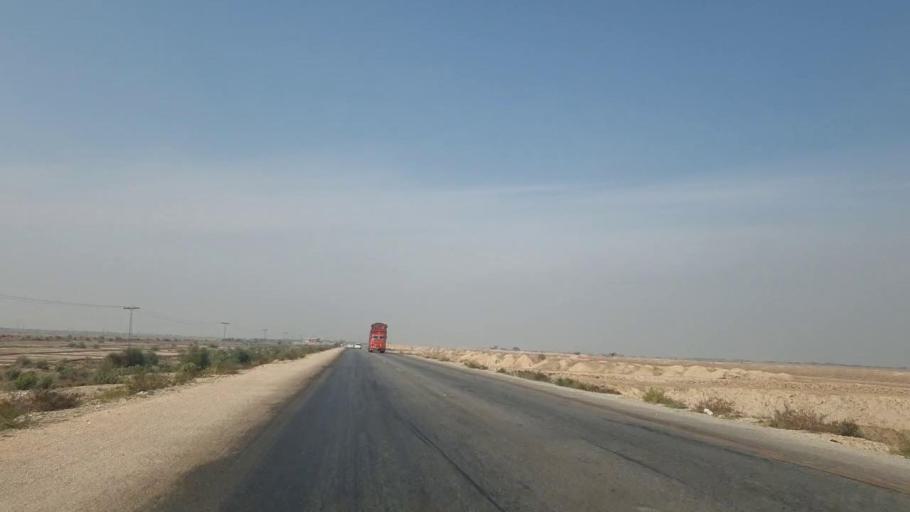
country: PK
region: Sindh
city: Sann
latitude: 25.9257
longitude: 68.2136
